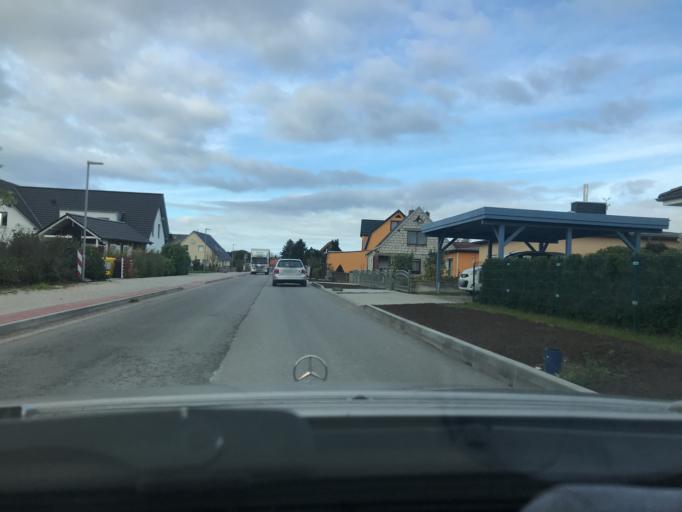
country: DE
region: Mecklenburg-Vorpommern
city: Ostseebad Zinnowitz
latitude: 54.0646
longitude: 13.9051
